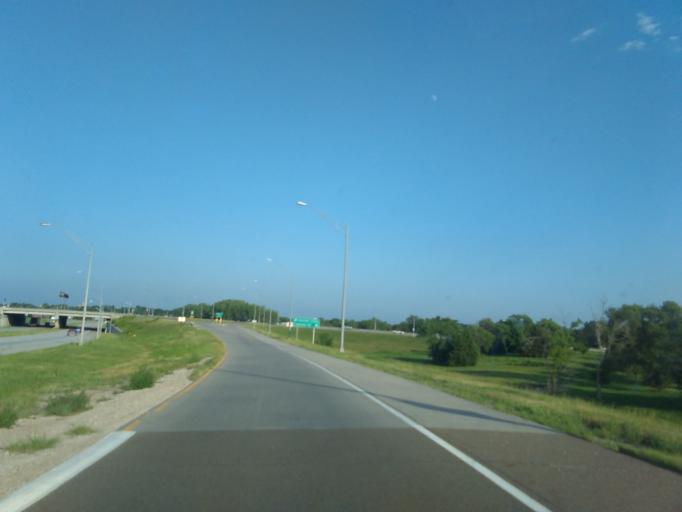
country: US
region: Nebraska
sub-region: Lancaster County
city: Lincoln
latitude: 40.8036
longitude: -96.7482
